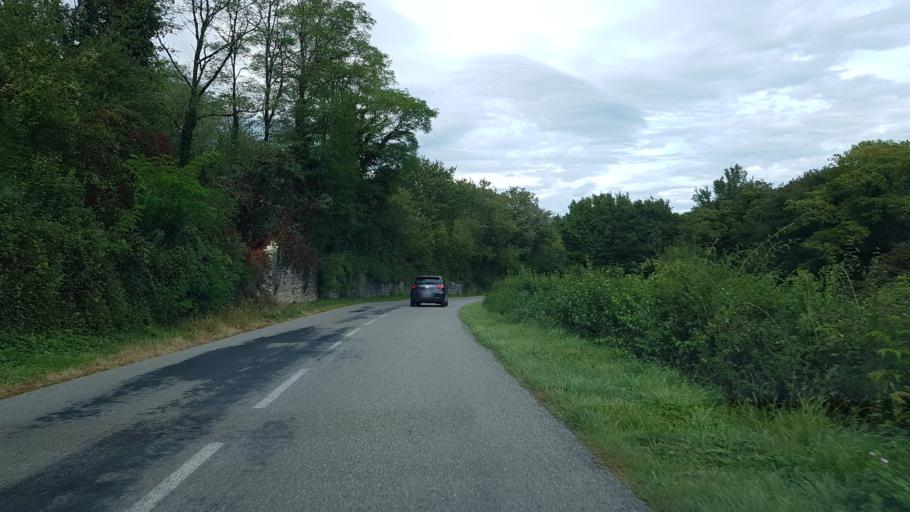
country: FR
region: Rhone-Alpes
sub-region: Departement de l'Ain
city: Villereversure
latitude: 46.1739
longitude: 5.3680
